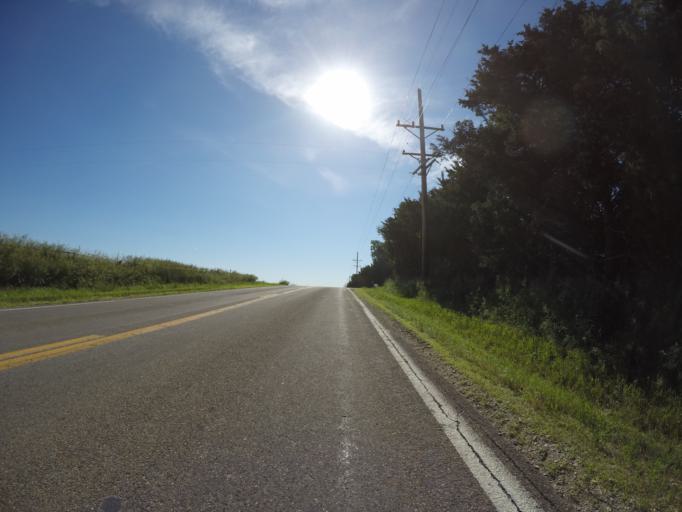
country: US
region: Kansas
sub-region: Mitchell County
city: Beloit
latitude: 39.6393
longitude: -97.9441
